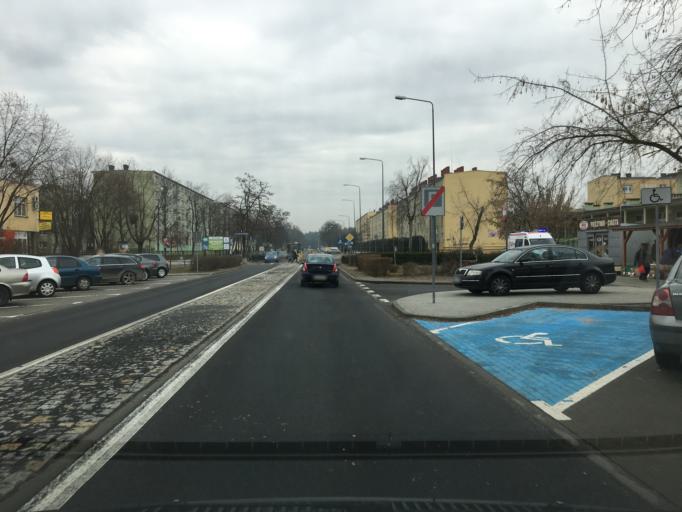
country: PL
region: Opole Voivodeship
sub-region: Powiat kedzierzynsko-kozielski
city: Kedzierzyn-Kozle
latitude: 50.3455
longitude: 18.2200
